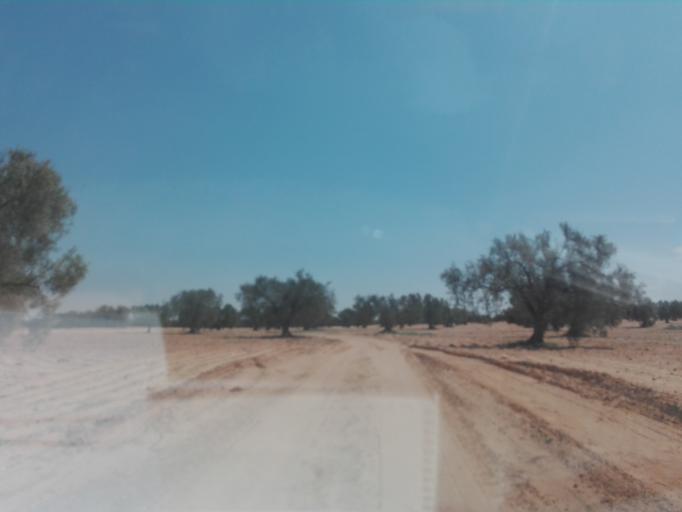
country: TN
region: Safaqis
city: Bi'r `Ali Bin Khalifah
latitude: 34.6109
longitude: 10.3447
